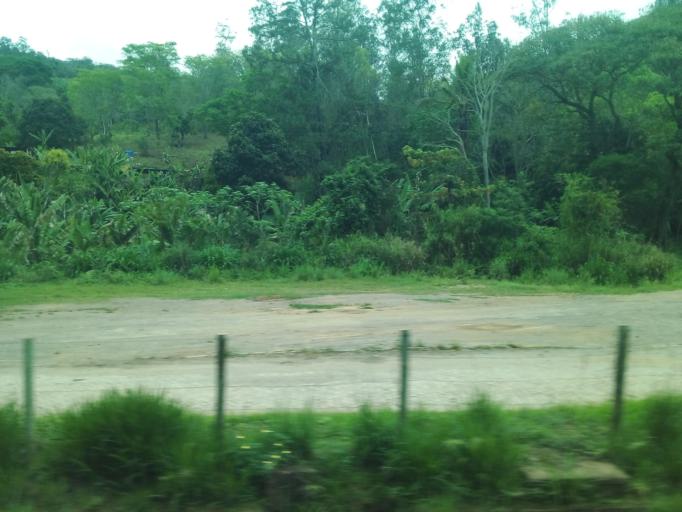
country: BR
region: Minas Gerais
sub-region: Nova Era
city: Nova Era
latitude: -19.7256
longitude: -42.9917
